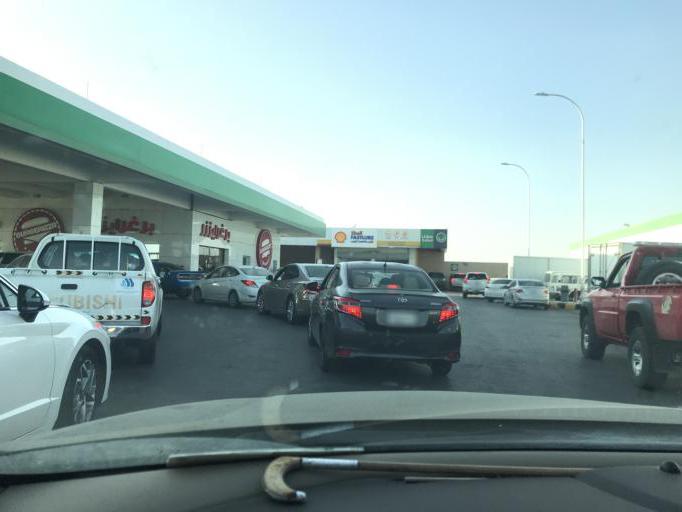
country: SA
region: Ar Riyad
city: Riyadh
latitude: 24.9285
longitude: 46.7138
